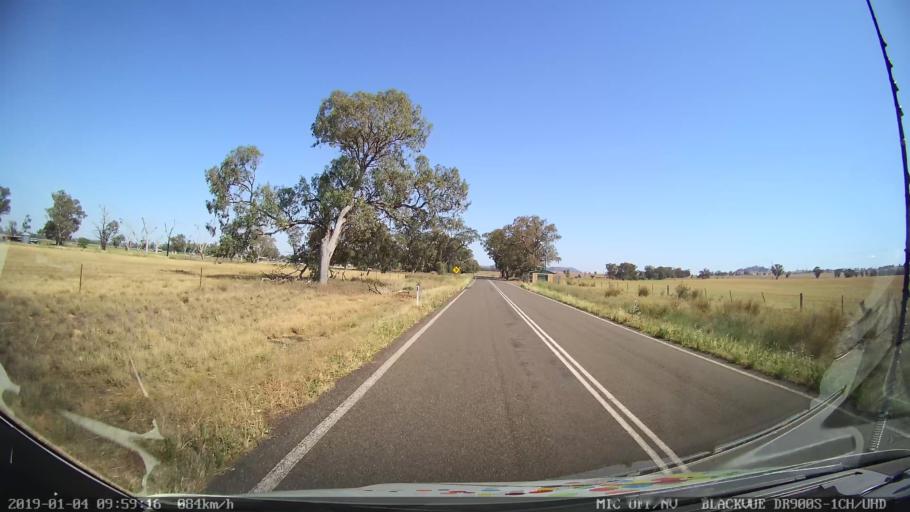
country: AU
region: New South Wales
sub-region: Cabonne
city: Canowindra
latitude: -33.5094
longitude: 148.3874
